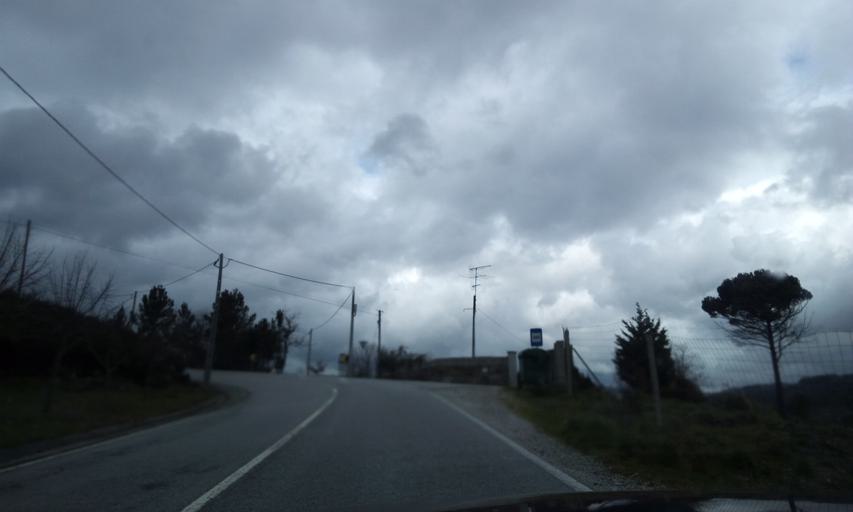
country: PT
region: Viseu
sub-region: Viseu
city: Rio de Loba
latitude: 40.6108
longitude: -7.8644
